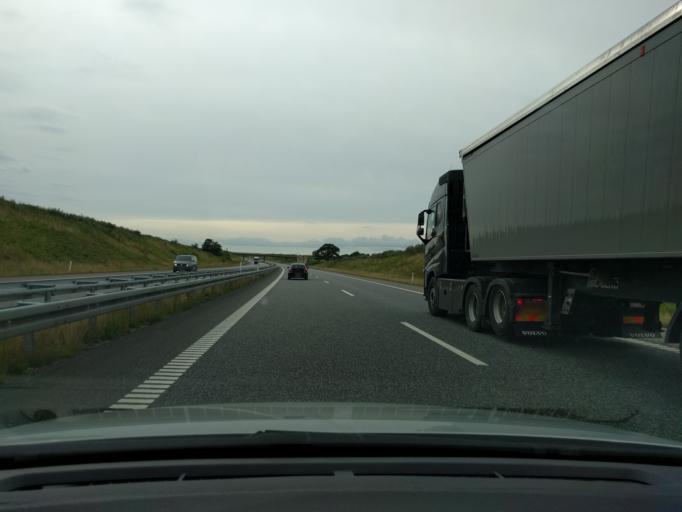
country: DK
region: Central Jutland
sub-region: Hedensted Kommune
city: Torring
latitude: 55.8326
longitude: 9.5053
